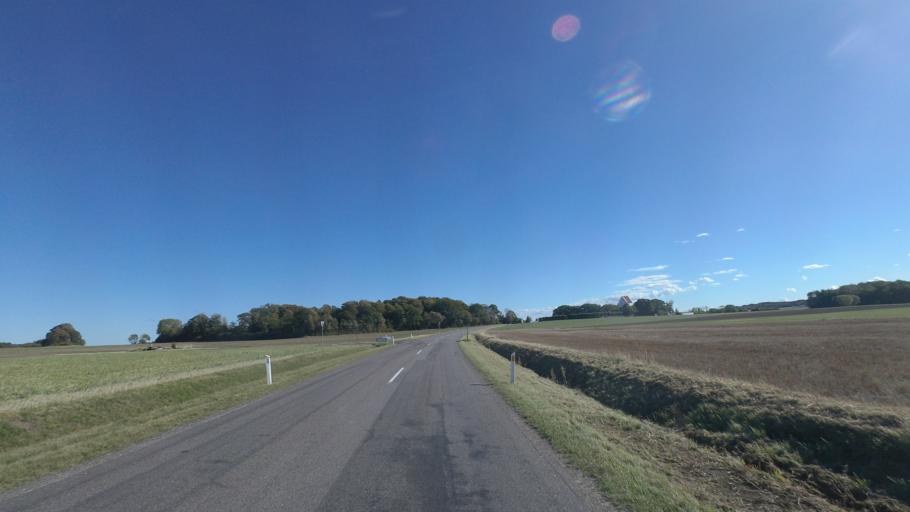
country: DK
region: Capital Region
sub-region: Bornholm Kommune
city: Nexo
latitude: 55.1206
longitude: 15.1019
